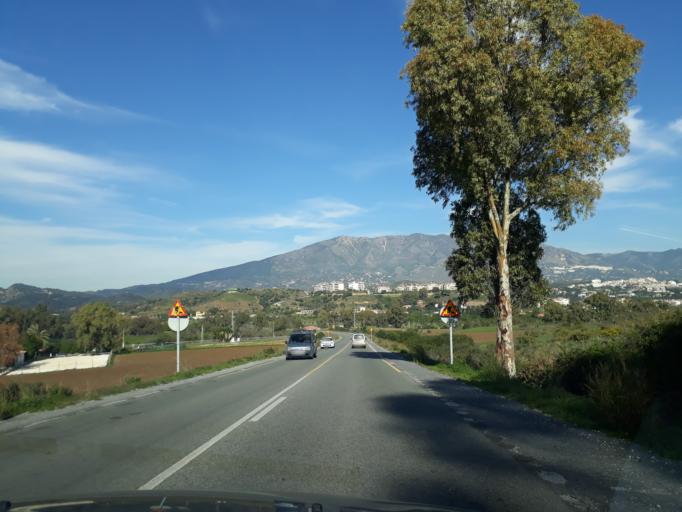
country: ES
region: Andalusia
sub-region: Provincia de Malaga
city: Fuengirola
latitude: 36.5394
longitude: -4.6875
